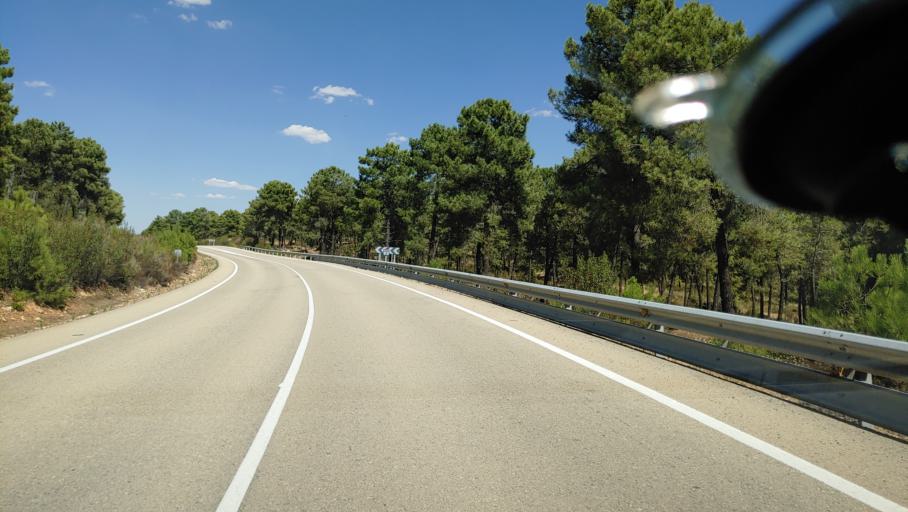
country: ES
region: Castille-La Mancha
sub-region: Provincia de Ciudad Real
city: Saceruela
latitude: 38.9992
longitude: -4.5156
